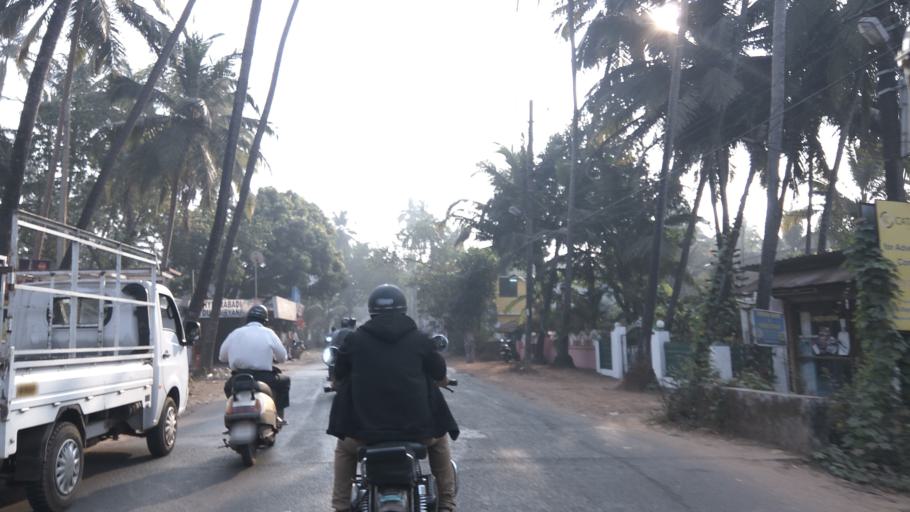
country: IN
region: Goa
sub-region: North Goa
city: Saligao
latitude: 15.5461
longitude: 73.7925
